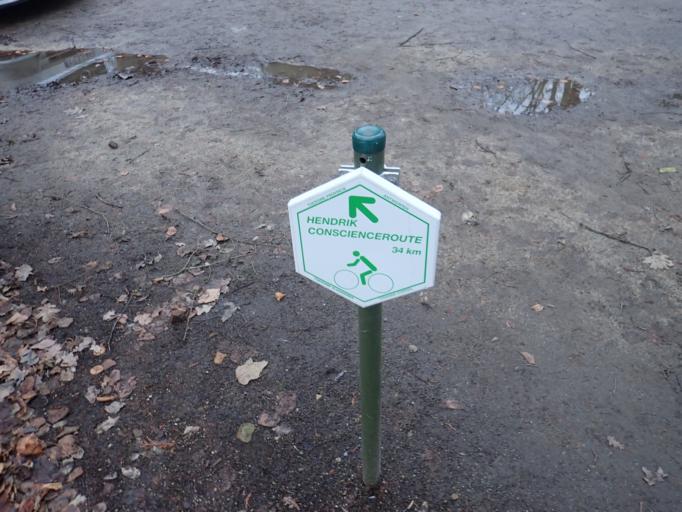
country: BE
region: Flanders
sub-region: Provincie Antwerpen
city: Schilde
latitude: 51.2488
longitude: 4.6282
